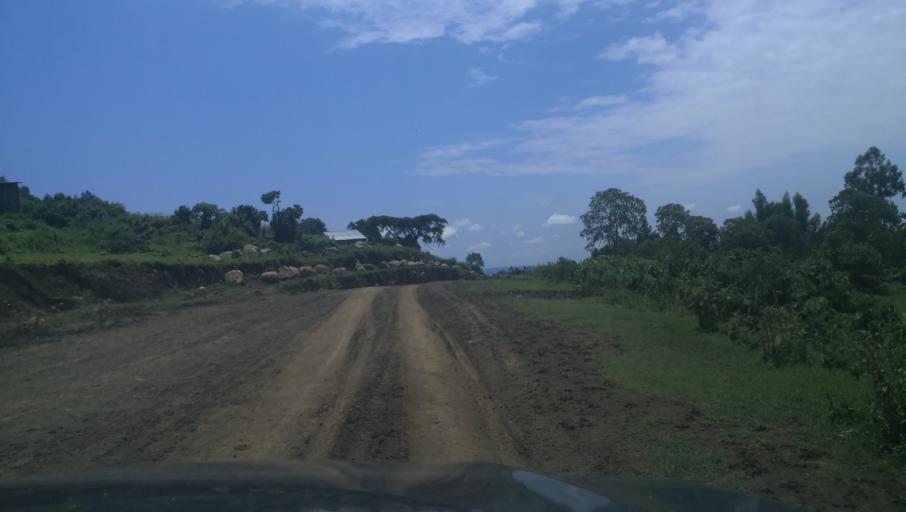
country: ET
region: Southern Nations, Nationalities, and People's Region
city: Butajira
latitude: 8.2754
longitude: 38.4826
